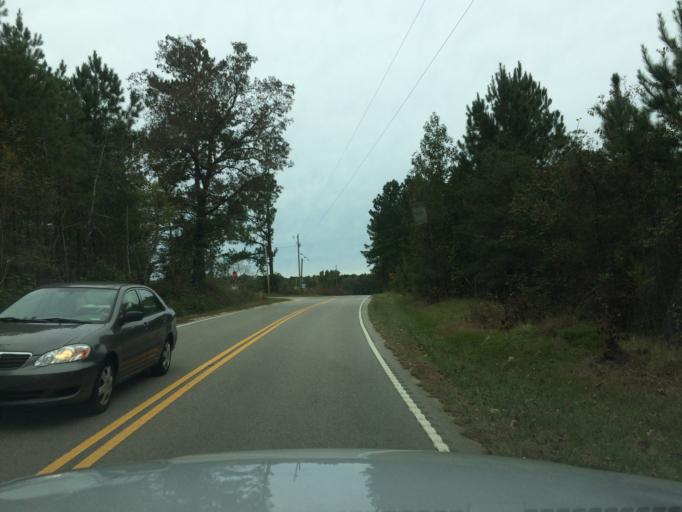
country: US
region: South Carolina
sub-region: Aiken County
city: New Ellenton
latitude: 33.4635
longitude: -81.6774
